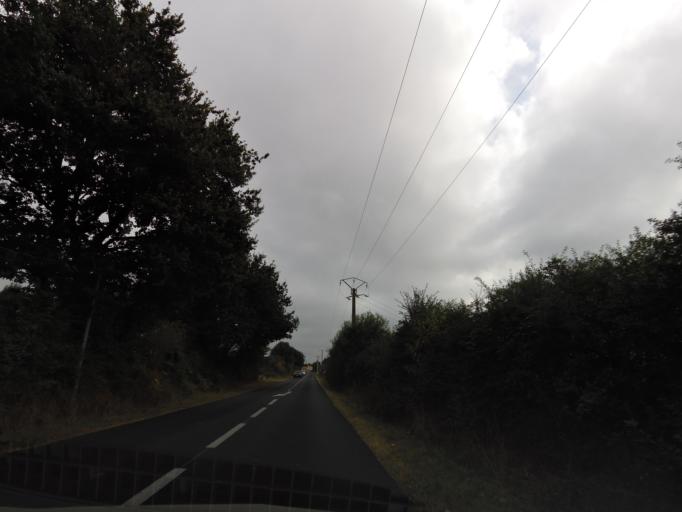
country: FR
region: Pays de la Loire
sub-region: Departement de la Vendee
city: Avrille
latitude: 46.4634
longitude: -1.4539
